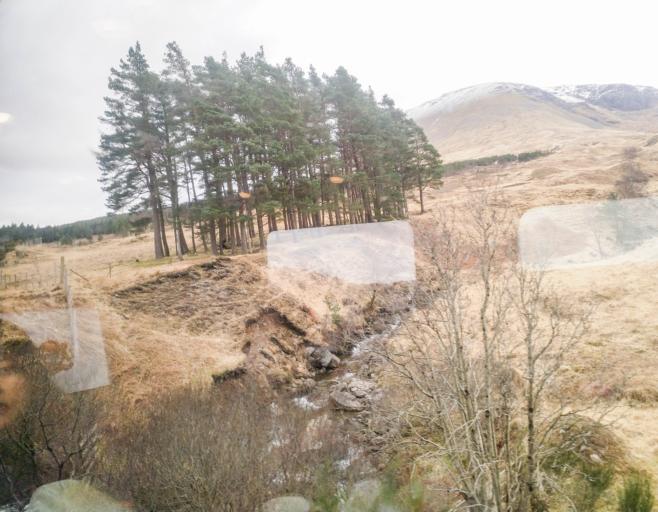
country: GB
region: Scotland
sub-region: Highland
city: Spean Bridge
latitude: 56.5183
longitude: -4.7647
